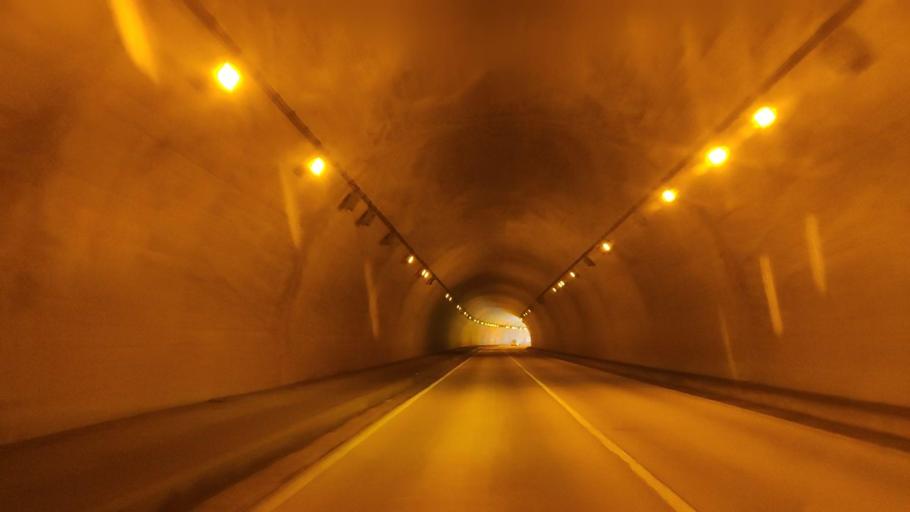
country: JP
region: Ishikawa
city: Nanao
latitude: 37.3835
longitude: 137.2335
